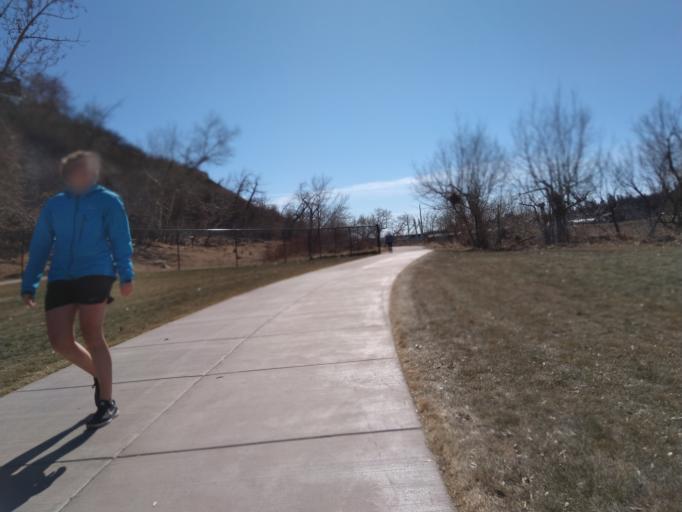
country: CA
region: Alberta
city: Calgary
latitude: 51.0356
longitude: -114.0495
